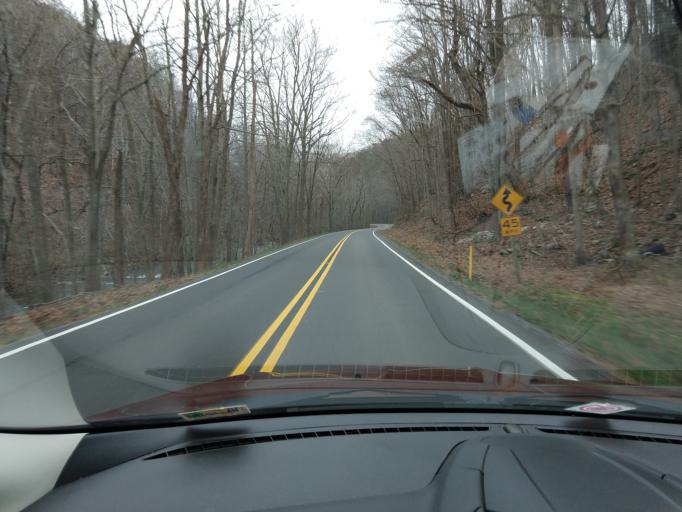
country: US
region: West Virginia
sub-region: Greenbrier County
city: White Sulphur Springs
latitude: 37.7259
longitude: -80.2224
